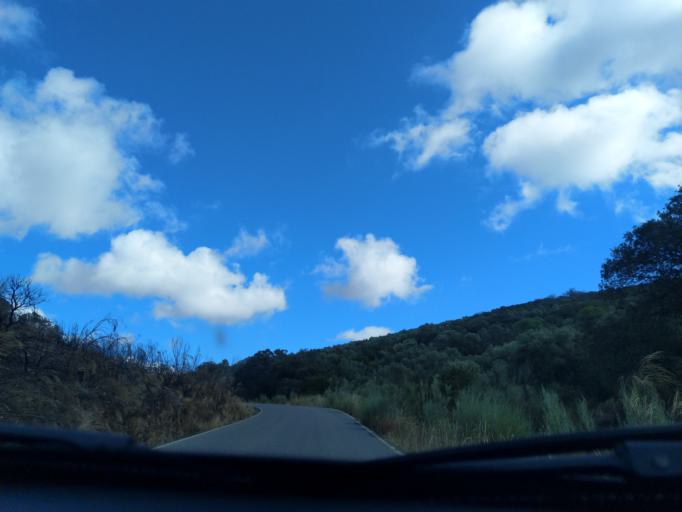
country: ES
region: Extremadura
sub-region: Provincia de Badajoz
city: Reina
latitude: 38.1448
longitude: -5.9146
